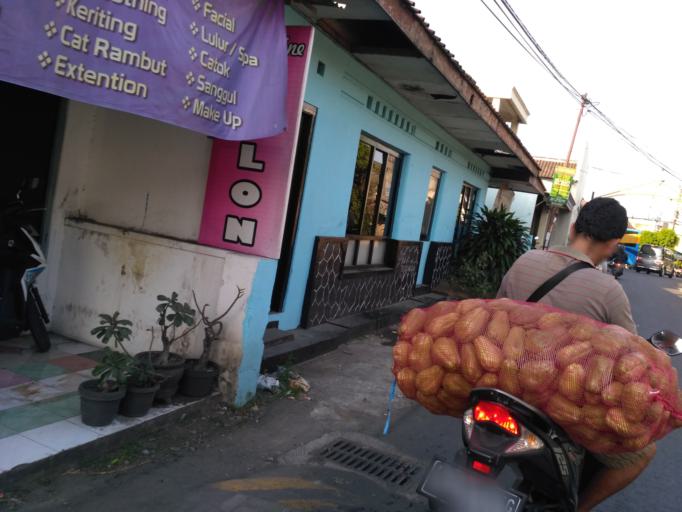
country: ID
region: Daerah Istimewa Yogyakarta
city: Sewon
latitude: -7.8339
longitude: 110.3901
